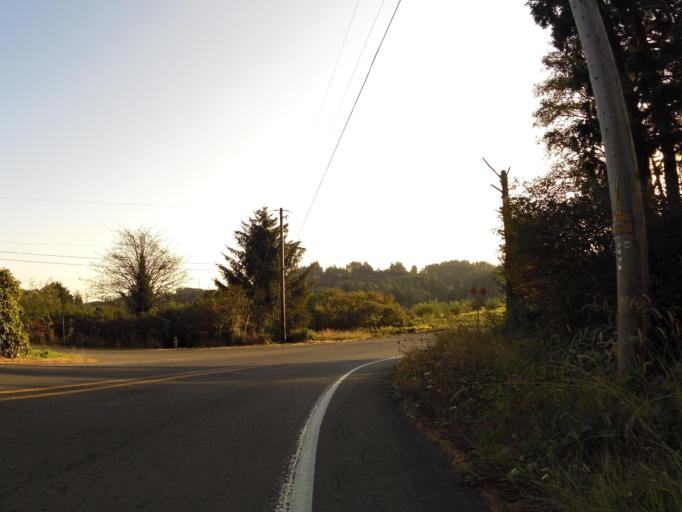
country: US
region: Oregon
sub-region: Lincoln County
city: Lincoln City
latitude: 44.9622
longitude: -123.9988
